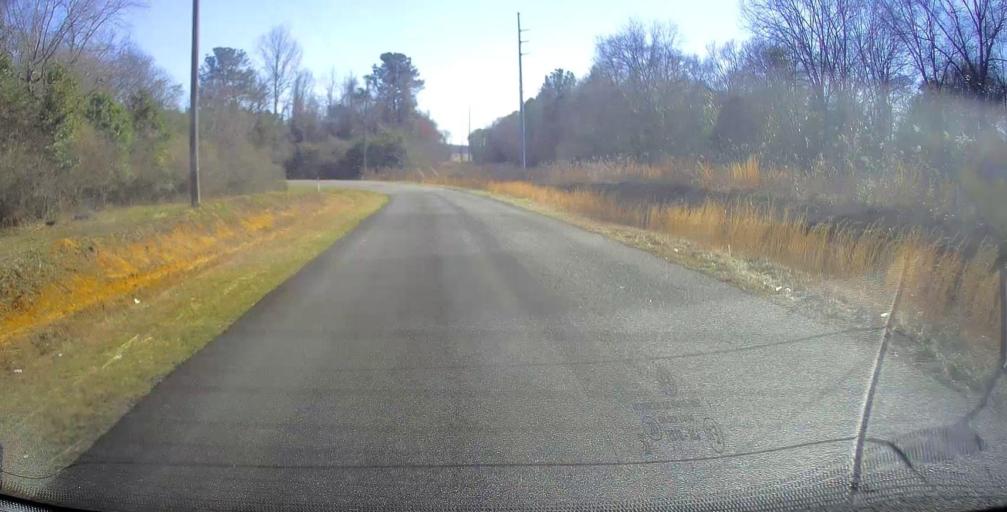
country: US
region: Georgia
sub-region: Crawford County
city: Roberta
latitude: 32.7166
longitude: -84.0089
